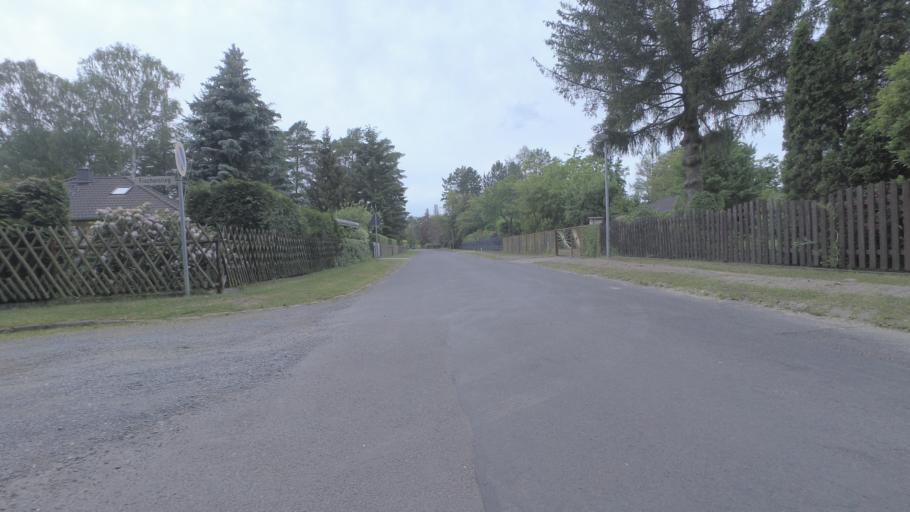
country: DE
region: Brandenburg
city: Bestensee
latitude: 52.2704
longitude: 13.7559
